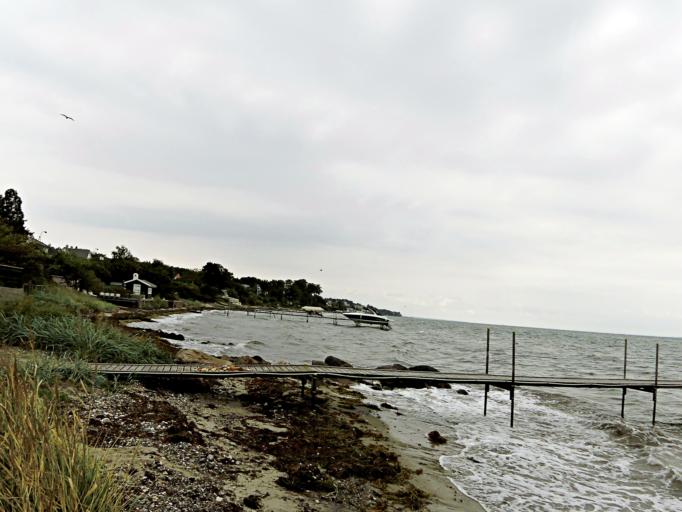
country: DK
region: Capital Region
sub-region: Rudersdal Kommune
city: Trorod
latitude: 55.8105
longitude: 12.5783
